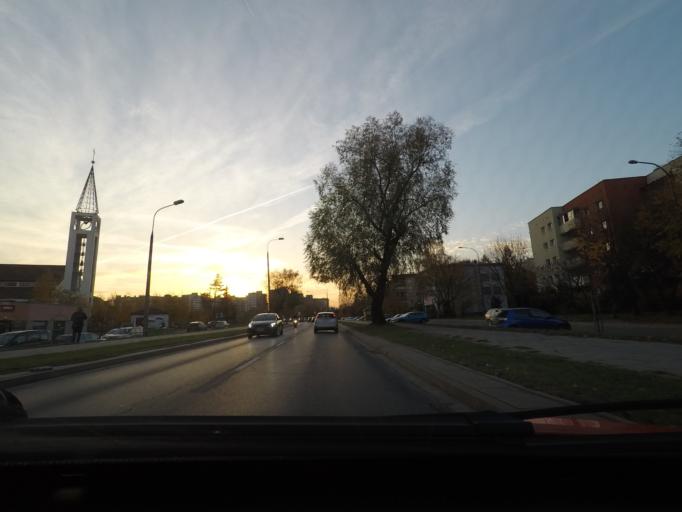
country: PL
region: Lesser Poland Voivodeship
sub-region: Krakow
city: Krakow
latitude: 50.0288
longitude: 19.9175
